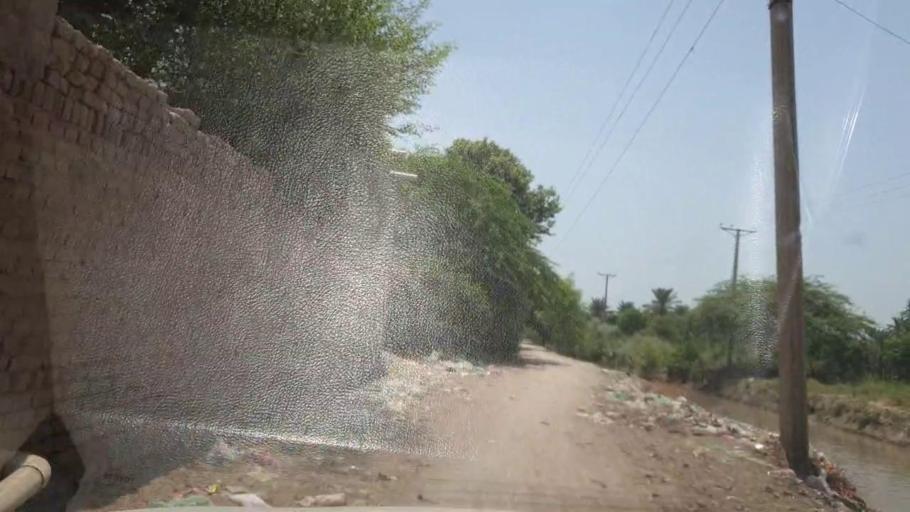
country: PK
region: Sindh
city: Bozdar
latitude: 27.1843
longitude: 68.6337
